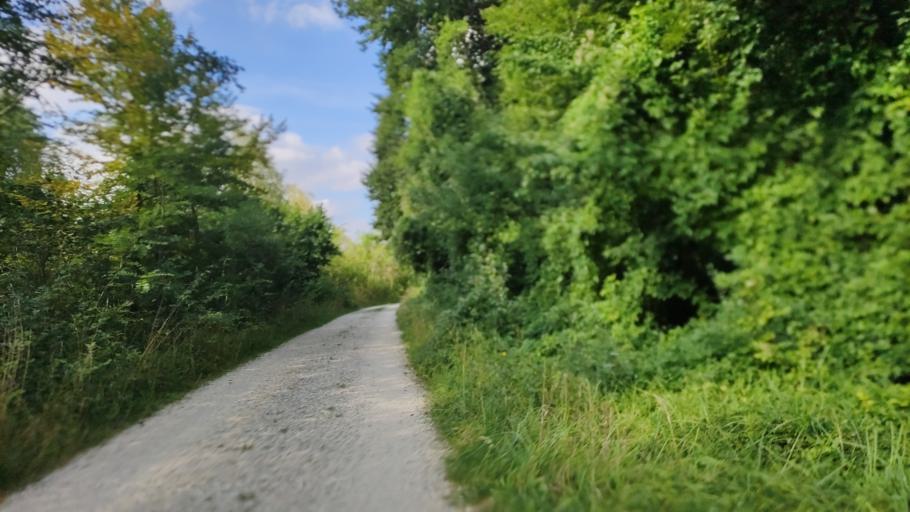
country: DE
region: Bavaria
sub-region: Upper Bavaria
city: Scheuring
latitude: 48.1449
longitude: 10.8683
